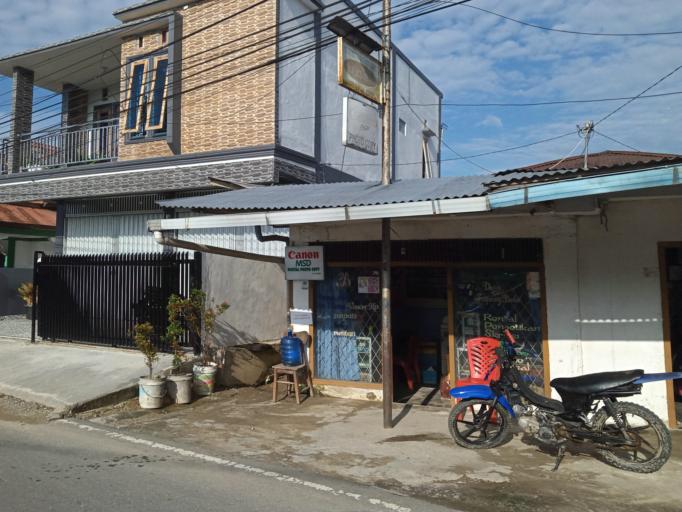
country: ID
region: Jambi
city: Semurup
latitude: -2.0087
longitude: 101.3764
